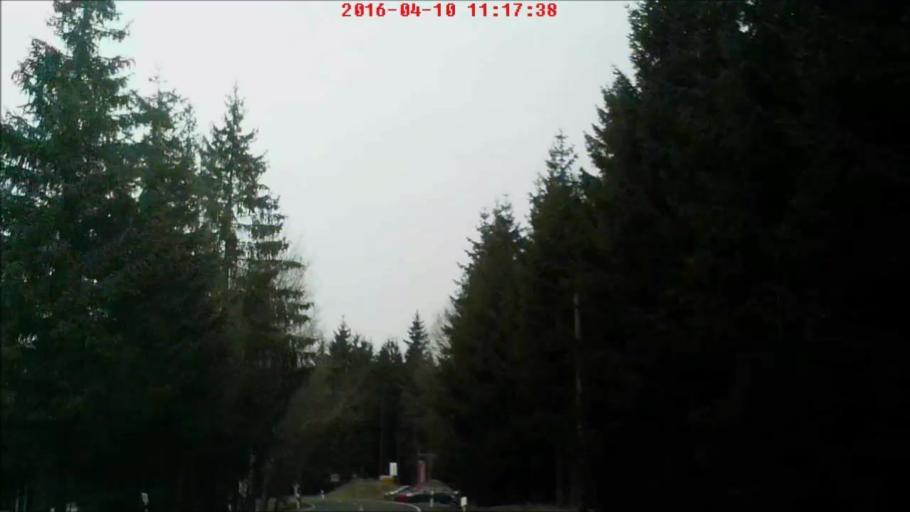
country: DE
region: Thuringia
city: Schmiedefeld am Rennsteig
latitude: 50.6146
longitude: 10.8371
